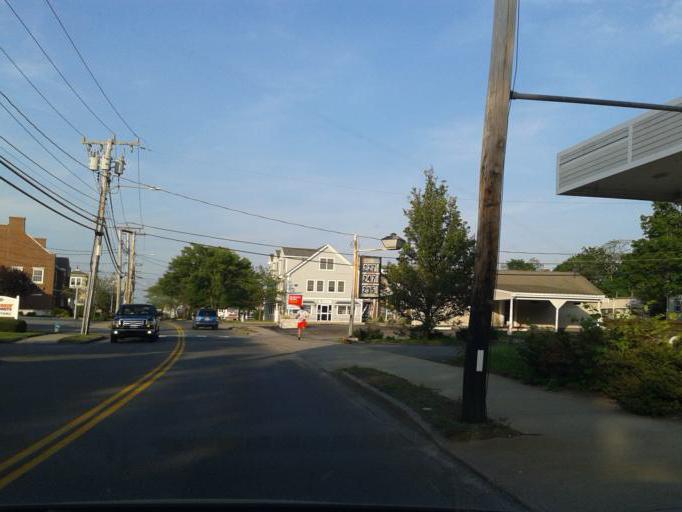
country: US
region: Massachusetts
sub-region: Barnstable County
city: Falmouth
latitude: 41.5524
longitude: -70.6062
